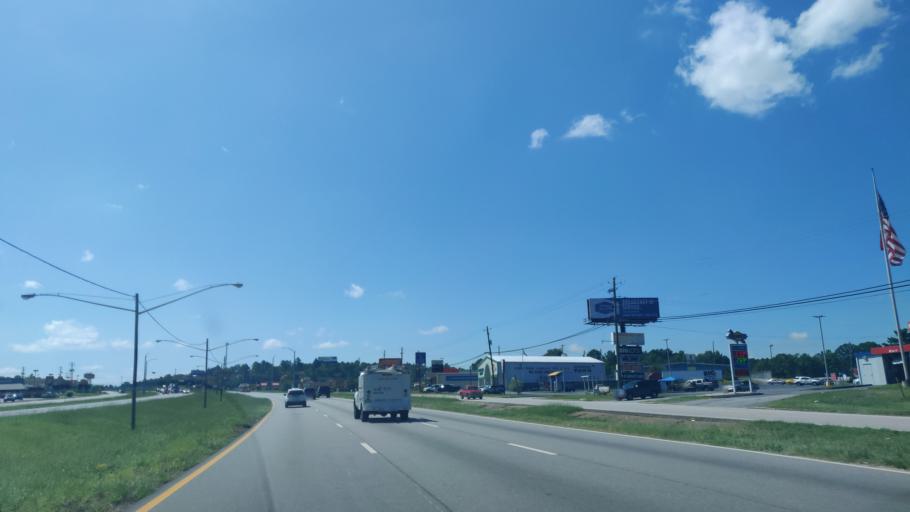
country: US
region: Alabama
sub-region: Russell County
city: Phenix City
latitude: 32.4686
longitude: -85.0286
